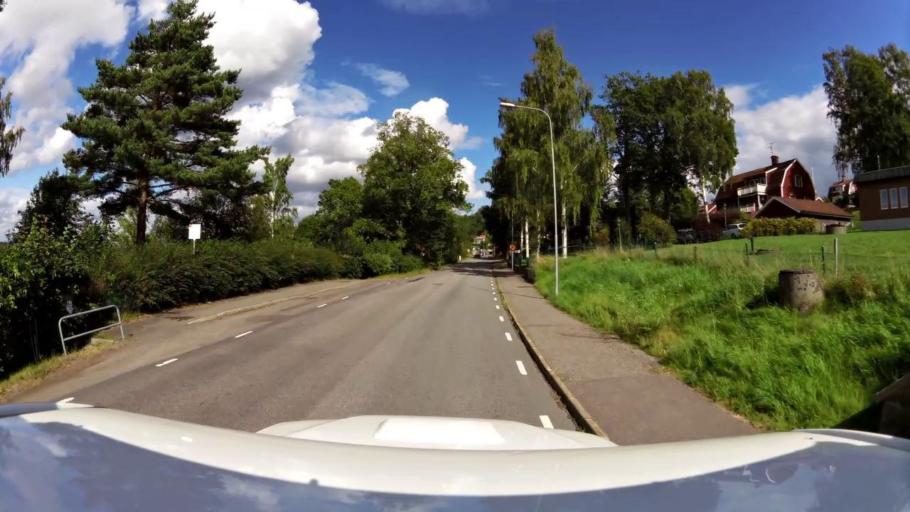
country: SE
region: OEstergoetland
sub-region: Kinda Kommun
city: Rimforsa
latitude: 58.2159
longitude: 15.6774
